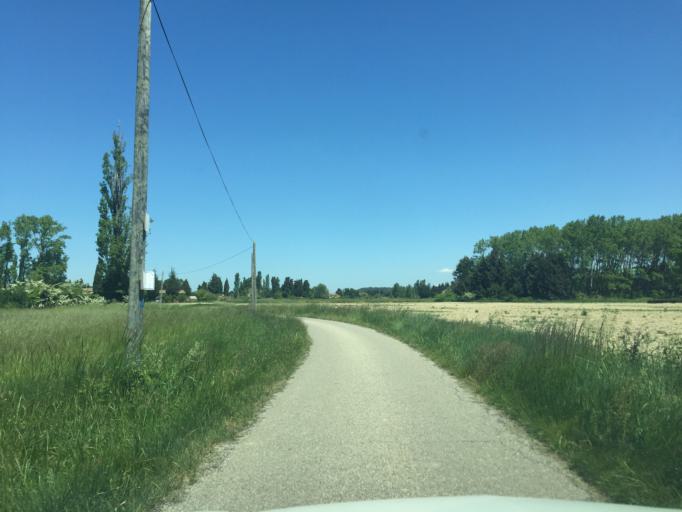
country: FR
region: Provence-Alpes-Cote d'Azur
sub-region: Departement du Vaucluse
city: Caderousse
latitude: 44.0999
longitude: 4.7839
